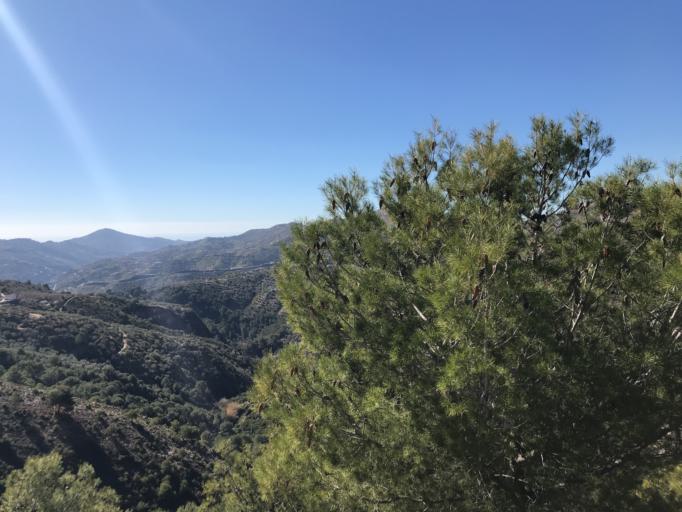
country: ES
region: Andalusia
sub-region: Provincia de Malaga
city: Canillas de Albaida
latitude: 36.8580
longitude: -3.9891
